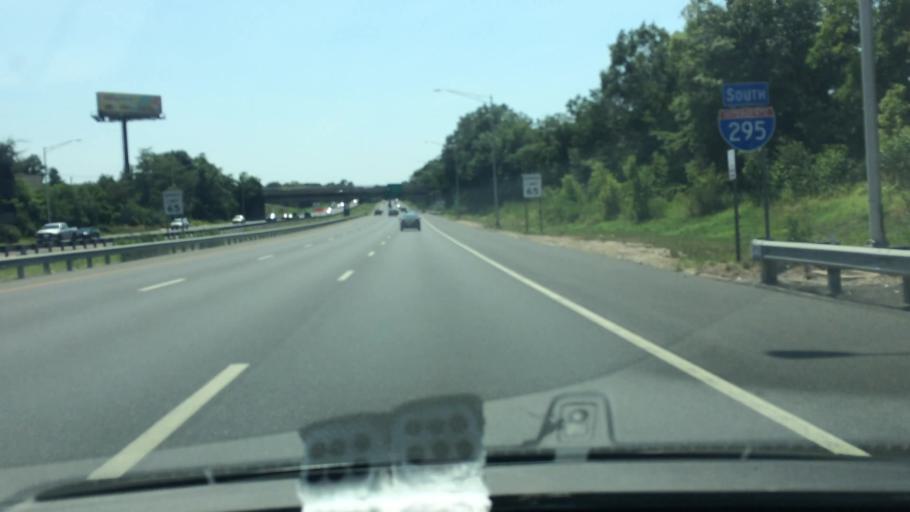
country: US
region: New Jersey
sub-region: Camden County
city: Bellmawr
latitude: 39.8647
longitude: -75.1078
